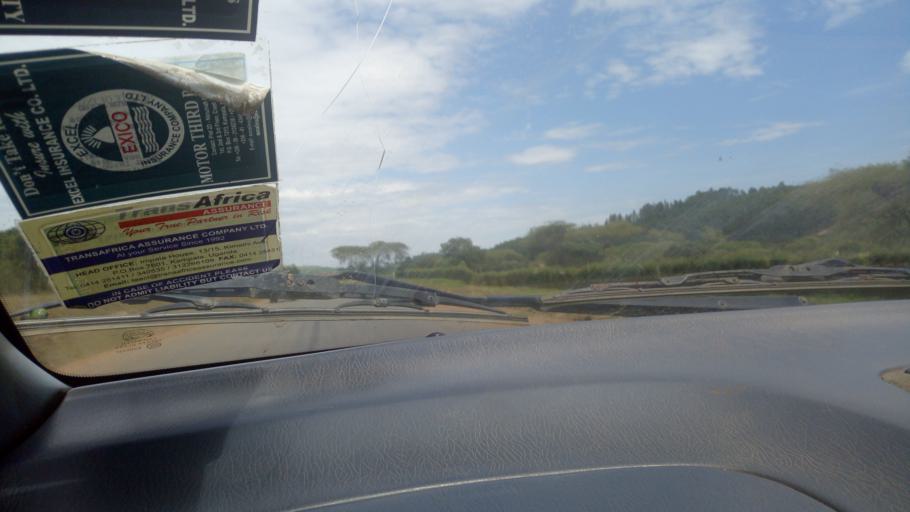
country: UG
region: Western Region
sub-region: Mbarara District
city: Bwizibwera
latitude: -0.3822
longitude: 30.5651
